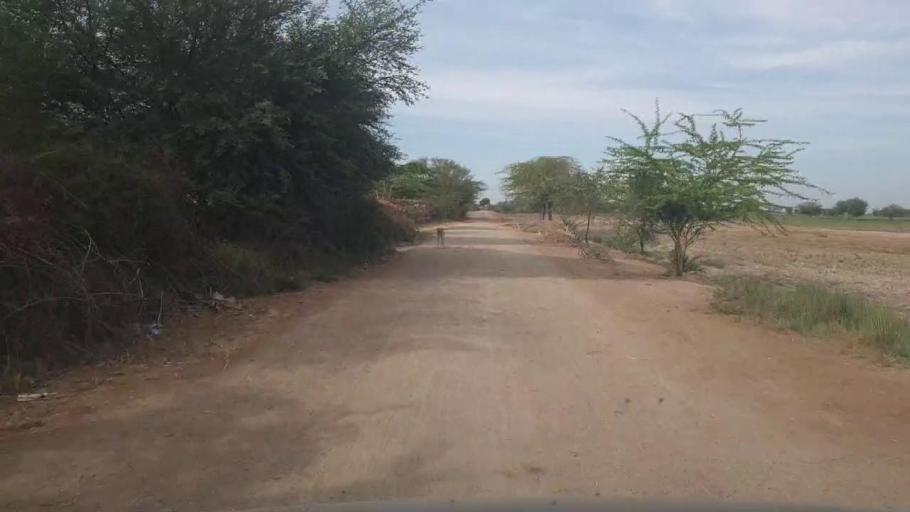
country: PK
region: Sindh
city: Kunri
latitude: 25.2759
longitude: 69.6035
